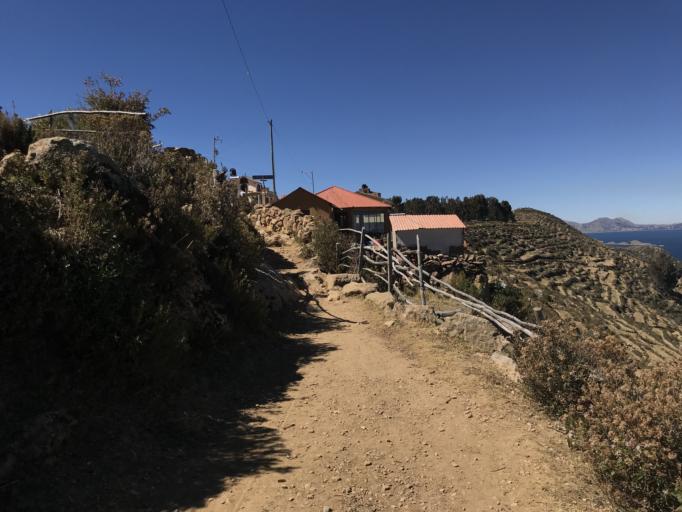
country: BO
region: La Paz
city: Yumani
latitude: -16.0348
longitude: -69.1518
